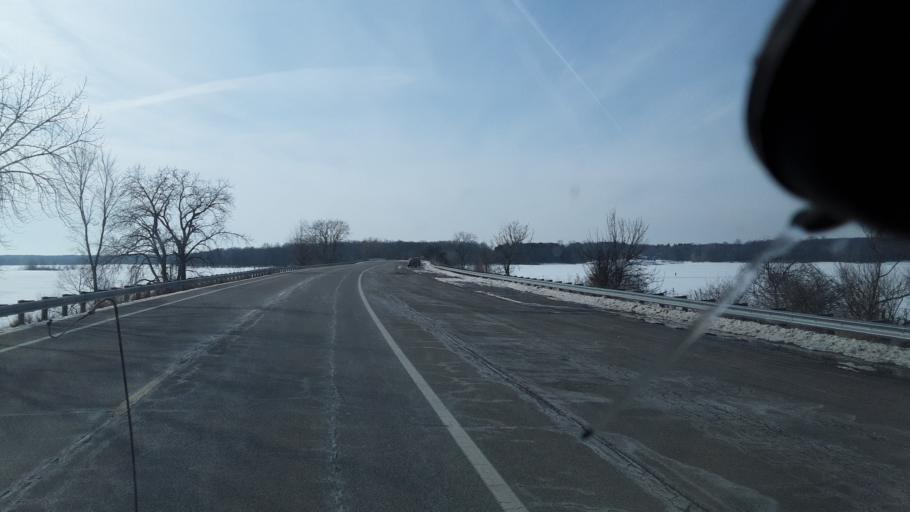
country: US
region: Ohio
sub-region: Mahoning County
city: Craig Beach
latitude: 41.0217
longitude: -80.9951
